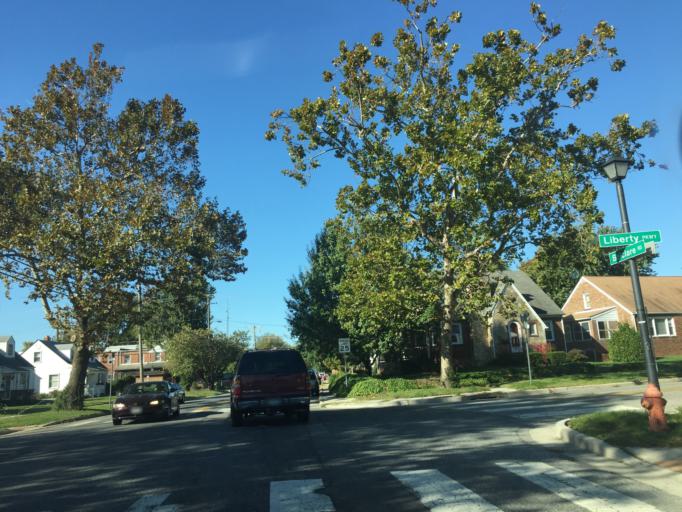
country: US
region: Maryland
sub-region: Baltimore County
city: Dundalk
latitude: 39.2519
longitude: -76.5143
